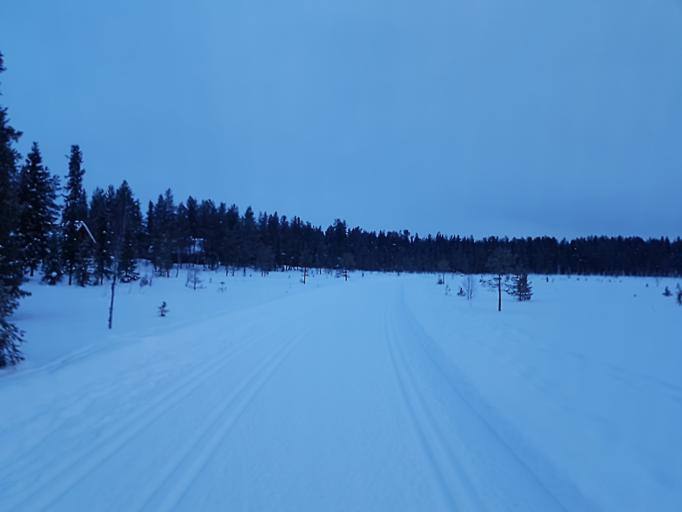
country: FI
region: Lapland
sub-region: Tunturi-Lappi
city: Kolari
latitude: 67.6164
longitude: 24.1412
